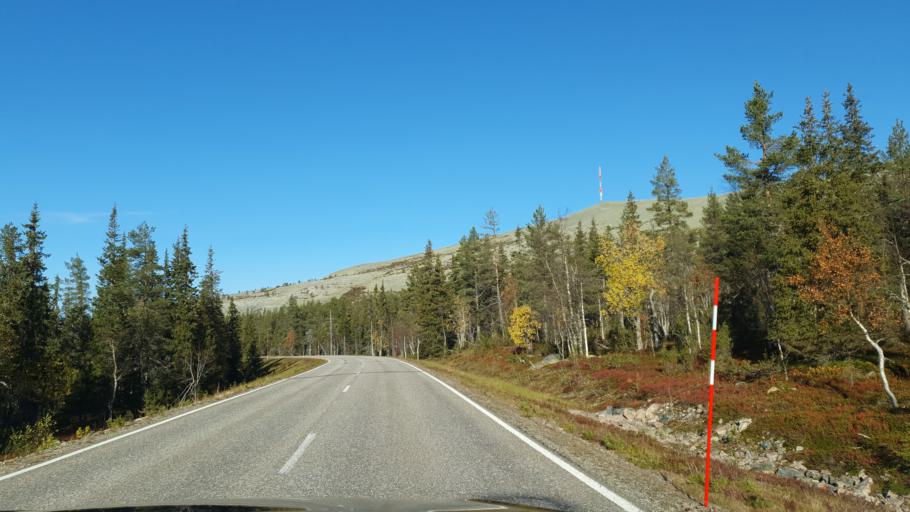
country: FI
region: Lapland
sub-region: Tunturi-Lappi
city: Kolari
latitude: 67.5513
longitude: 24.2094
